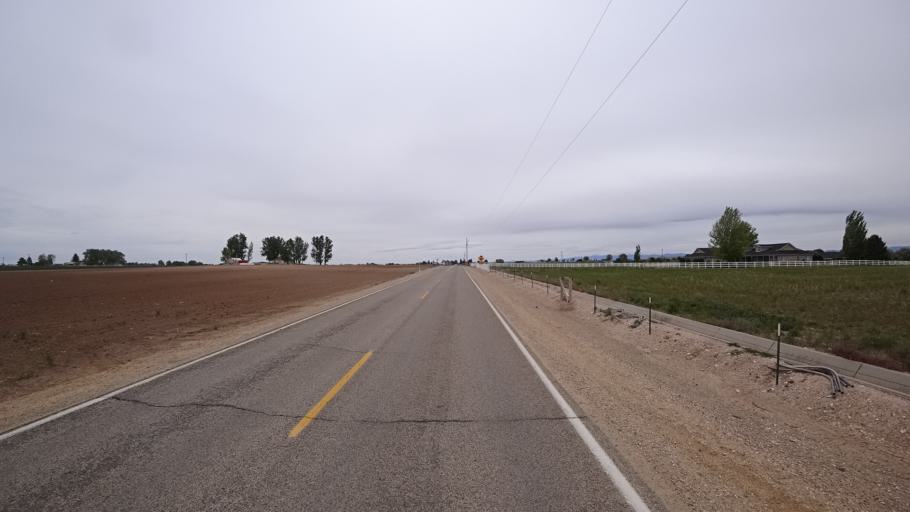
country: US
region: Idaho
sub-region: Ada County
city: Kuna
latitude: 43.5051
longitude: -116.3744
